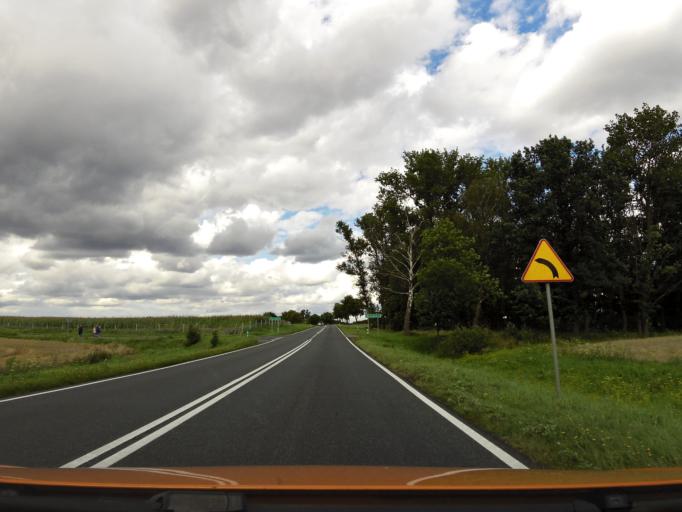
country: PL
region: West Pomeranian Voivodeship
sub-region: Powiat gryficki
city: Ploty
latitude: 53.7498
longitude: 15.2201
